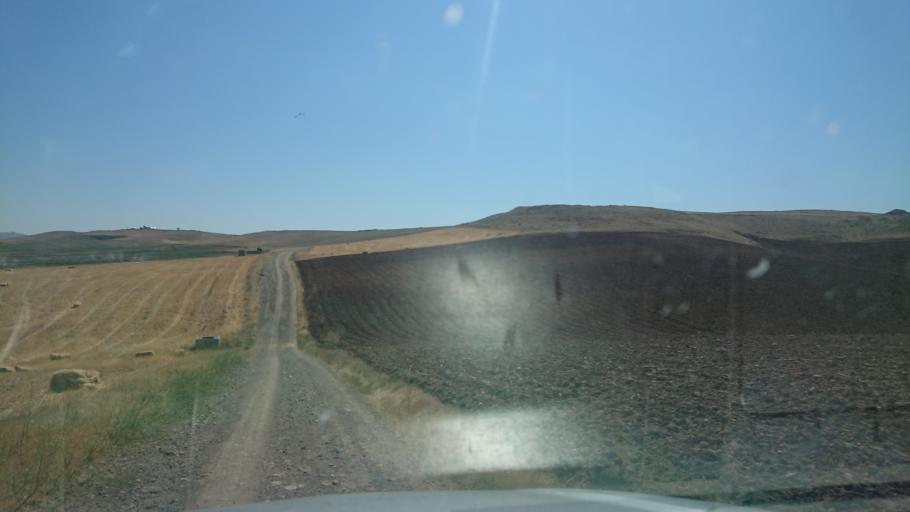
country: TR
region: Ankara
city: Evren
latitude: 39.0554
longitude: 33.8819
